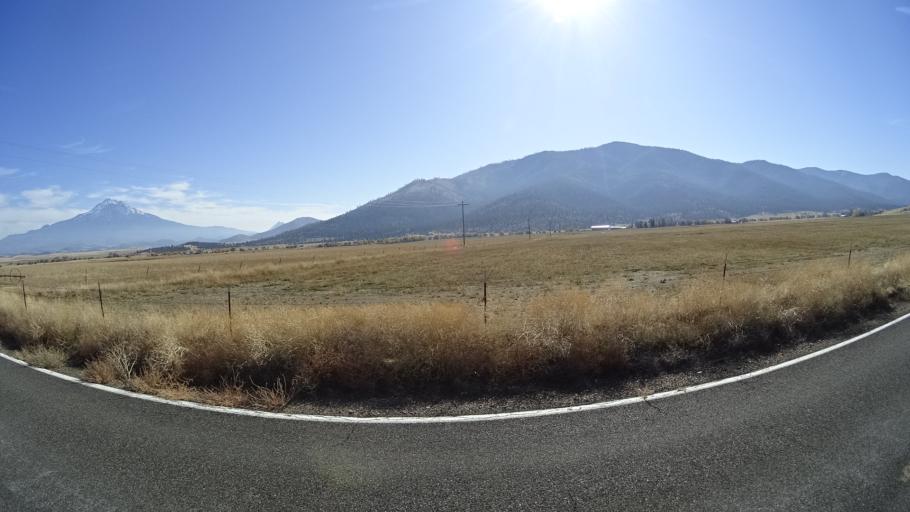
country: US
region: California
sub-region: Siskiyou County
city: Weed
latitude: 41.5062
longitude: -122.5419
